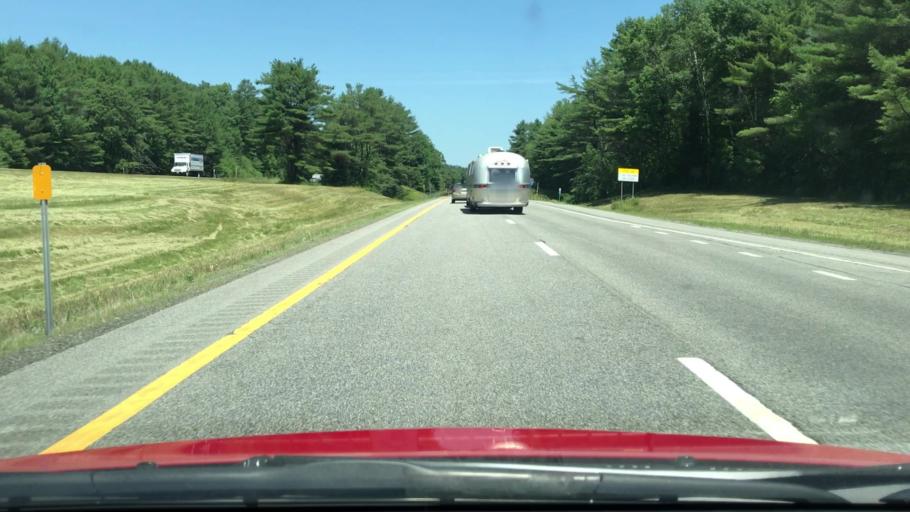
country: US
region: New York
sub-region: Essex County
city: Elizabethtown
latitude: 44.2909
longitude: -73.5317
